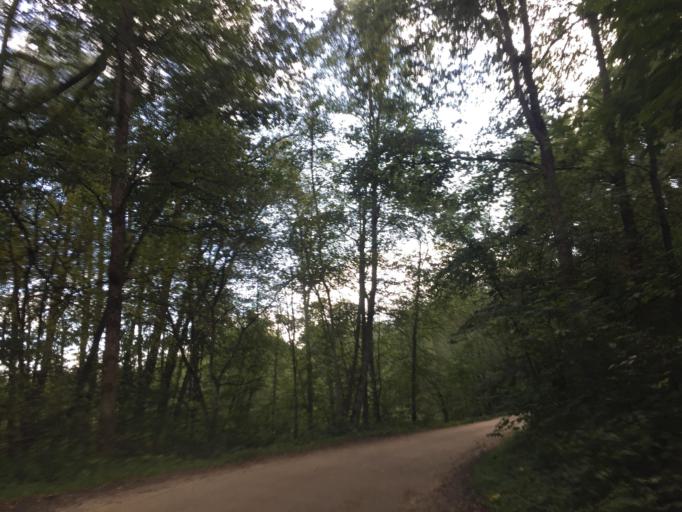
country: LV
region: Cesu Rajons
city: Cesis
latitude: 57.3209
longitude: 25.2227
